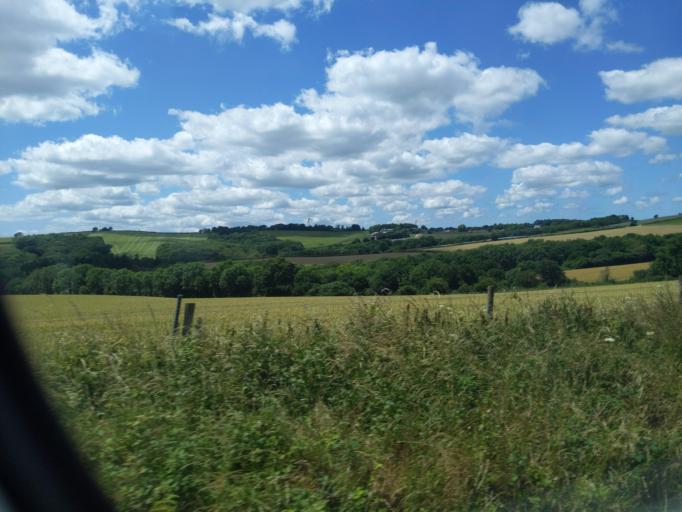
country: GB
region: England
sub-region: Cornwall
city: Pillaton
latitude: 50.4012
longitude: -4.3451
